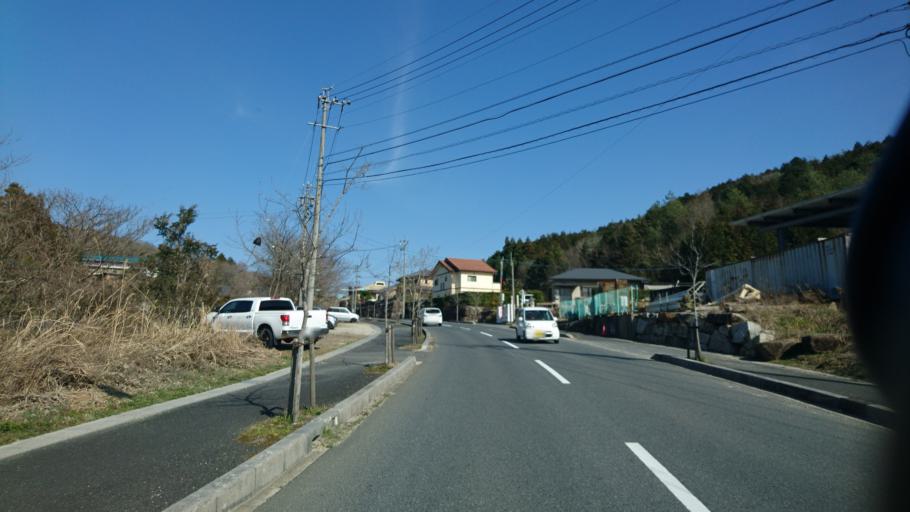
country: JP
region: Gifu
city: Nakatsugawa
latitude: 35.4643
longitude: 137.3878
